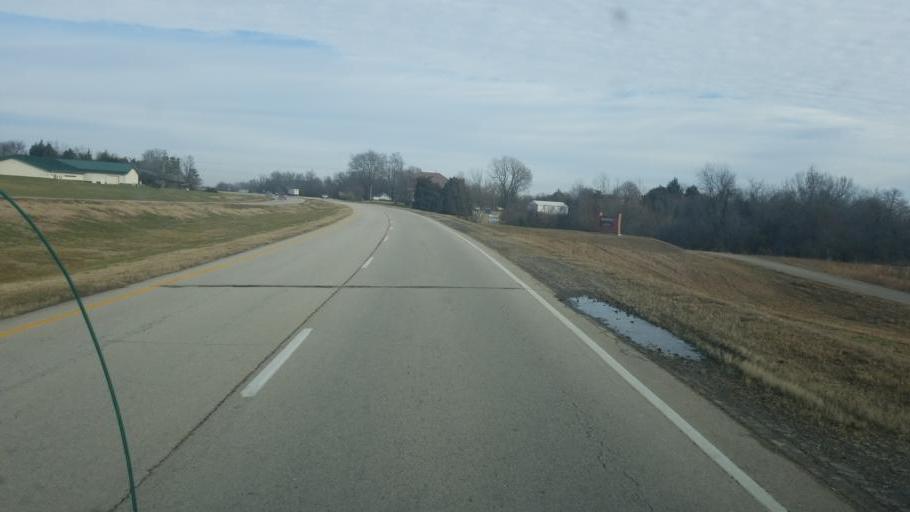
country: US
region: Missouri
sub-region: Stoddard County
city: Bloomfield
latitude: 36.8642
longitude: -89.9309
